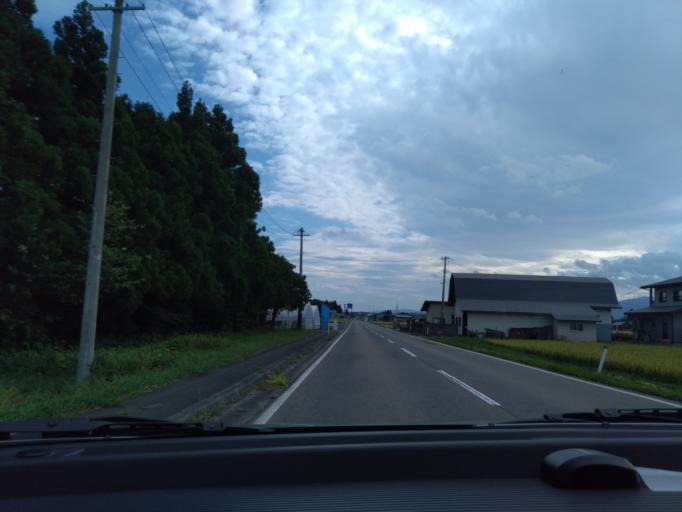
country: JP
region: Iwate
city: Kitakami
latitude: 39.3119
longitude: 141.0530
